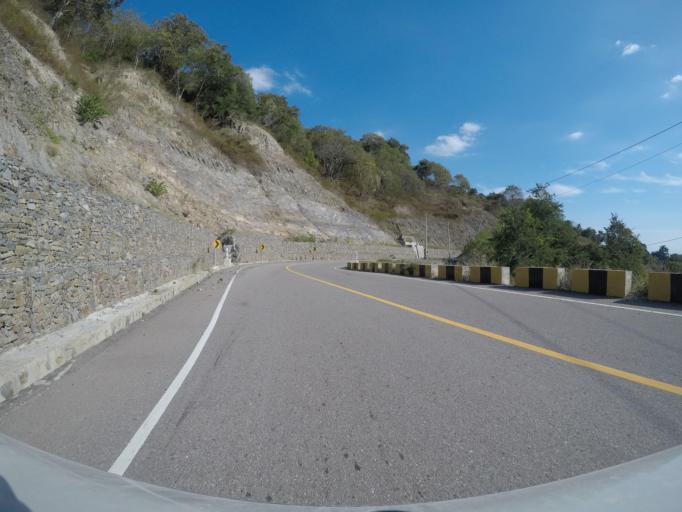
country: TL
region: Liquica
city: Maubara
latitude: -8.6508
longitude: 125.1215
